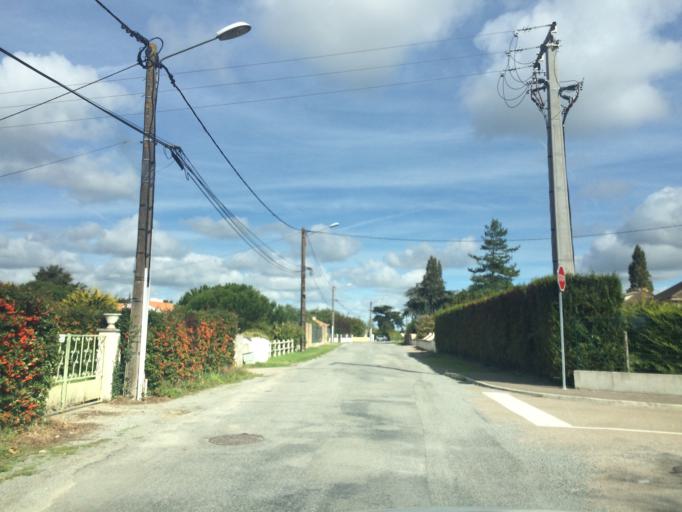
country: FR
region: Pays de la Loire
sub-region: Departement de la Loire-Atlantique
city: Chemere
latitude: 47.1177
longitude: -1.9235
